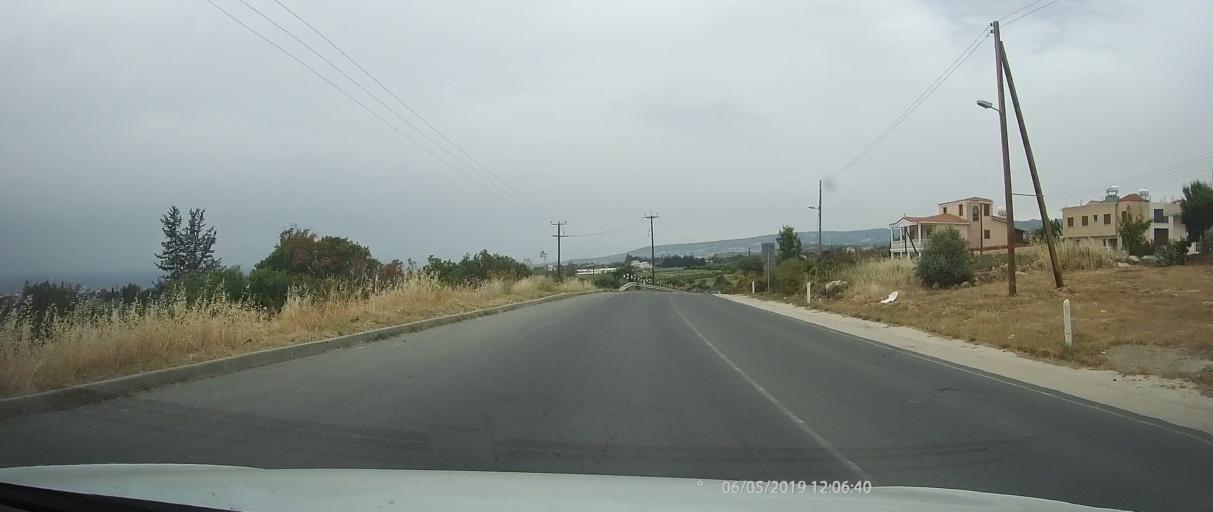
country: CY
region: Pafos
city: Empa
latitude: 34.8193
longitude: 32.4233
